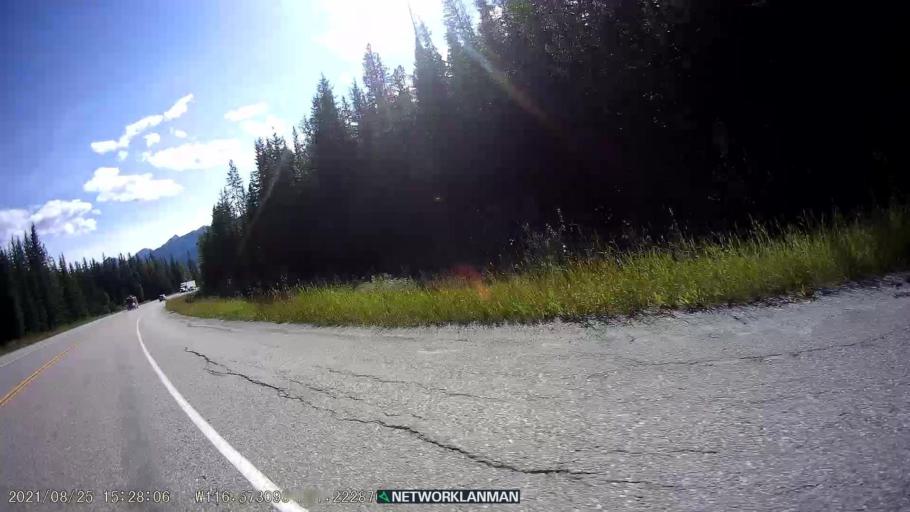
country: CA
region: Alberta
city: Lake Louise
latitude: 51.2224
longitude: -116.5733
